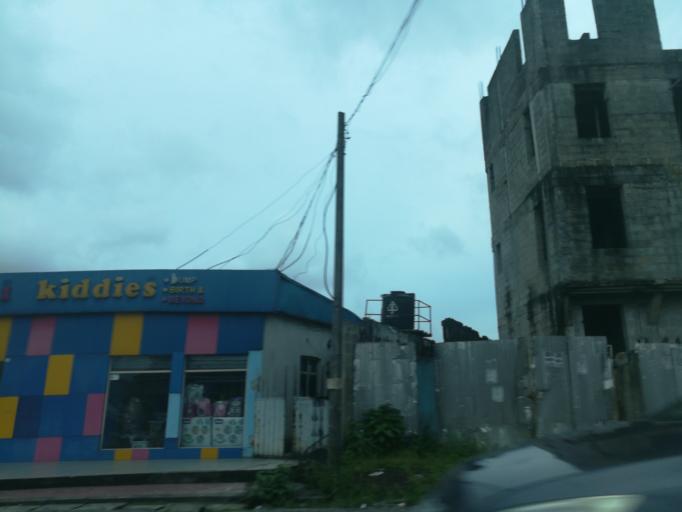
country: NG
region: Rivers
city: Port Harcourt
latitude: 4.8204
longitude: 7.0011
